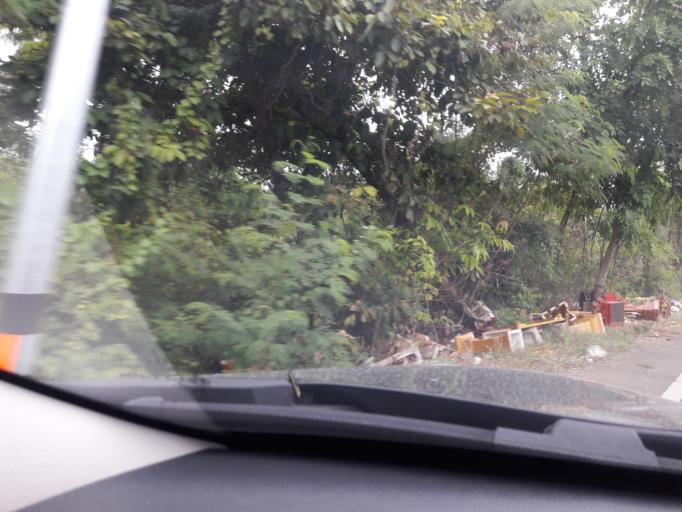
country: TH
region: Ratchaburi
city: Damnoen Saduak
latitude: 13.5942
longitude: 99.9452
